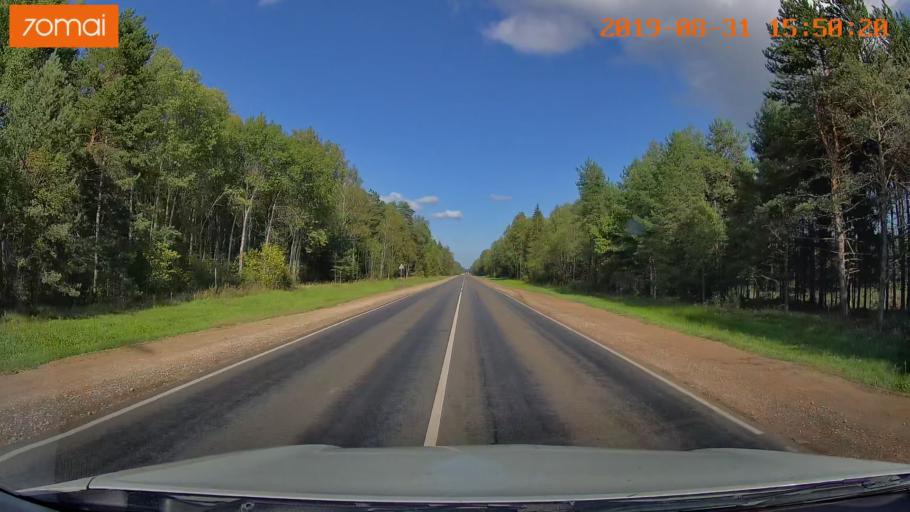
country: RU
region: Kaluga
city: Yukhnov
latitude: 54.6966
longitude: 35.0712
